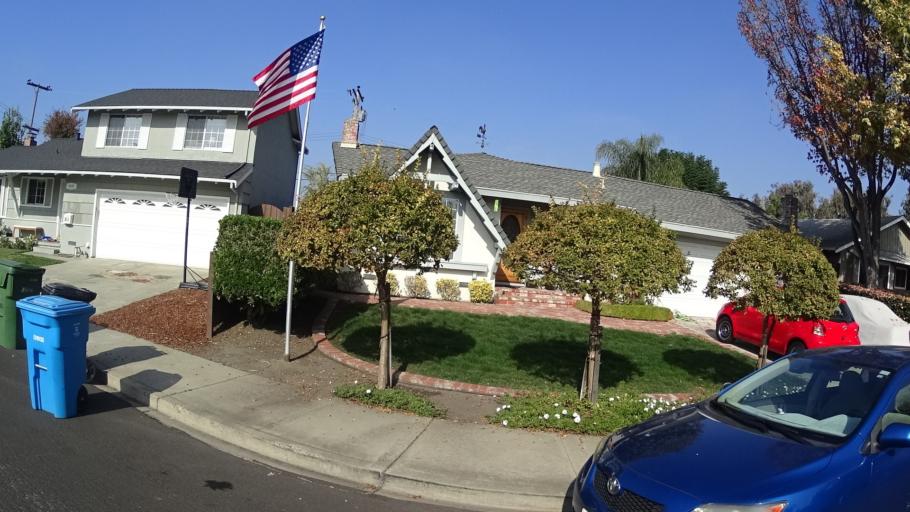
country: US
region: California
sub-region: Santa Clara County
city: Santa Clara
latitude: 37.3550
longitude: -121.9848
